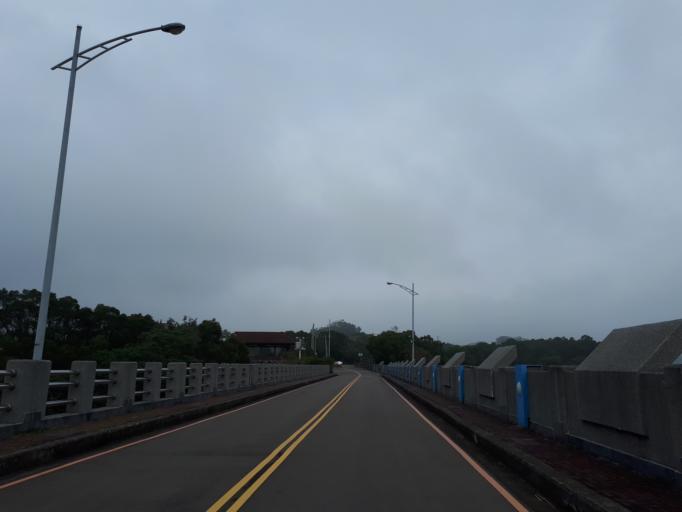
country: TW
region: Taiwan
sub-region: Hsinchu
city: Hsinchu
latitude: 24.7215
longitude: 121.0436
